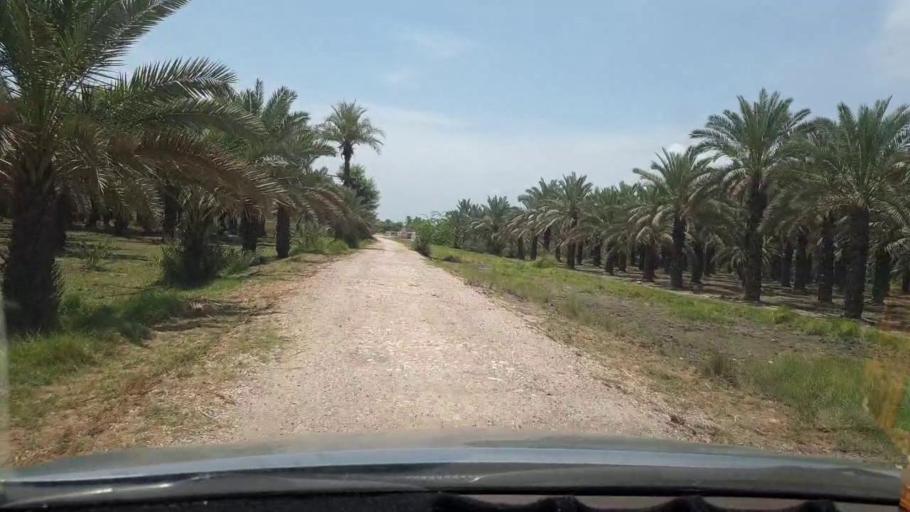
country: PK
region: Sindh
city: Khairpur
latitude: 27.4554
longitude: 68.7803
